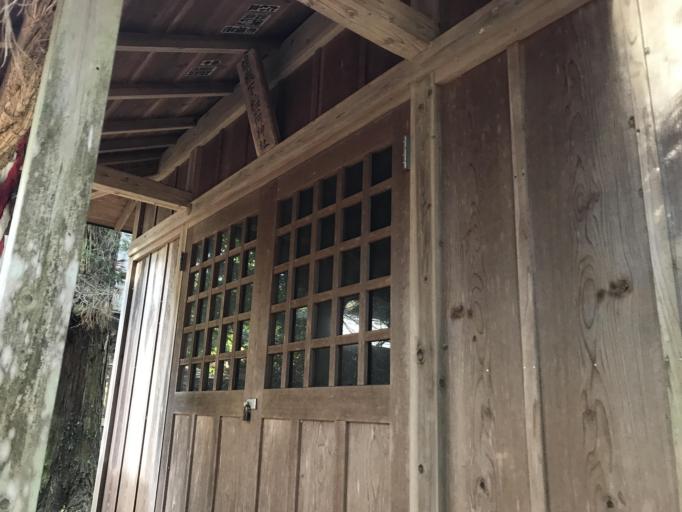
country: JP
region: Tochigi
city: Imaichi
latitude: 36.6750
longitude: 139.7238
